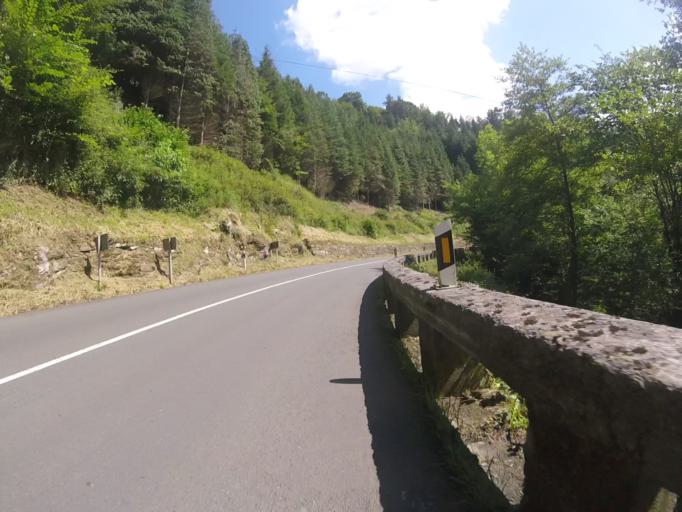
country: ES
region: Basque Country
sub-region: Provincia de Guipuzcoa
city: Errezil
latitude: 43.1748
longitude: -2.2149
